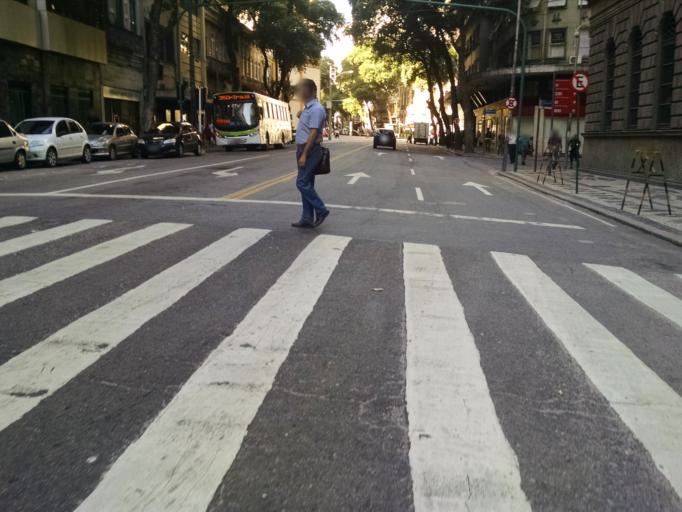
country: BR
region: Rio de Janeiro
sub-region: Rio De Janeiro
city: Rio de Janeiro
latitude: -22.8999
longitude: -43.1797
